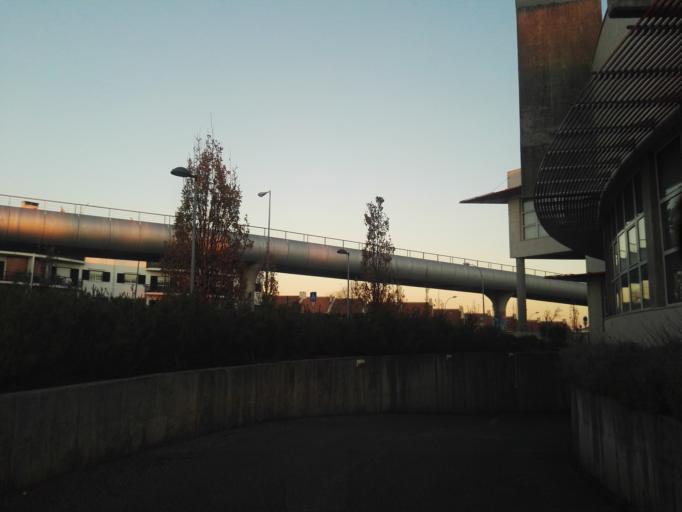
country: PT
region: Lisbon
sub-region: Oeiras
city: Paco de Arcos
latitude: 38.7035
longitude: -9.3011
